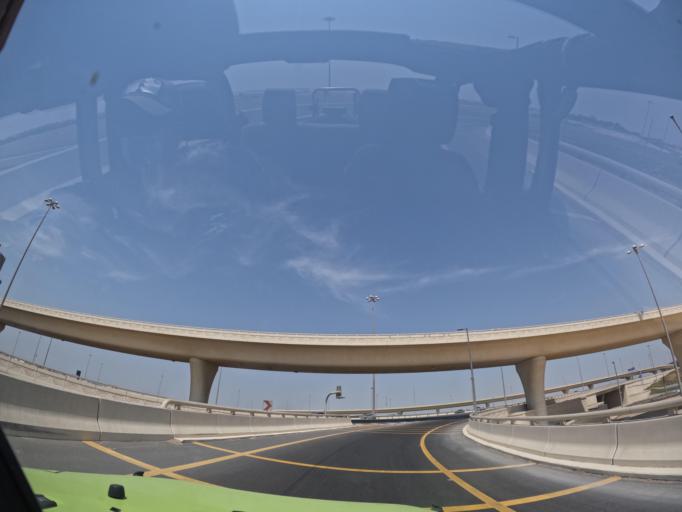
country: AE
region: Abu Dhabi
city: Abu Dhabi
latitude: 24.3074
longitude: 54.6008
